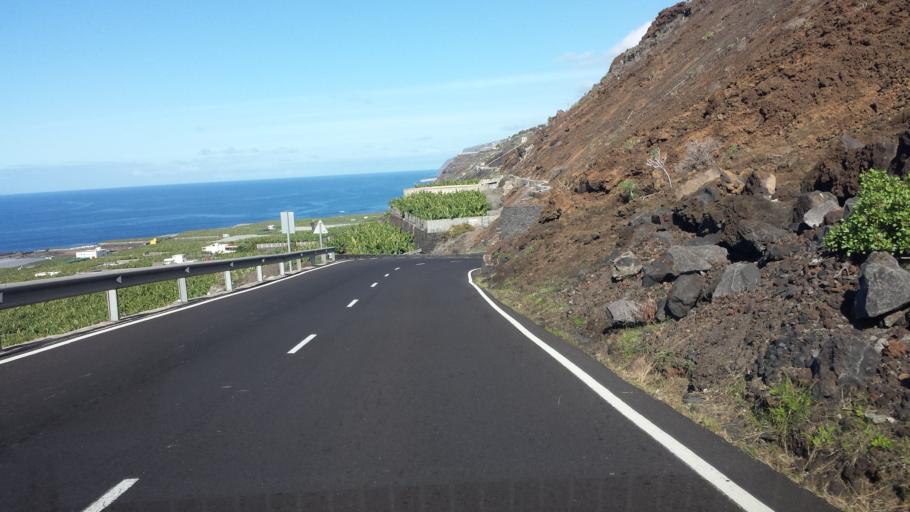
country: ES
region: Canary Islands
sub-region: Provincia de Santa Cruz de Tenerife
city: Tazacorte
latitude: 28.5922
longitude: -17.9111
